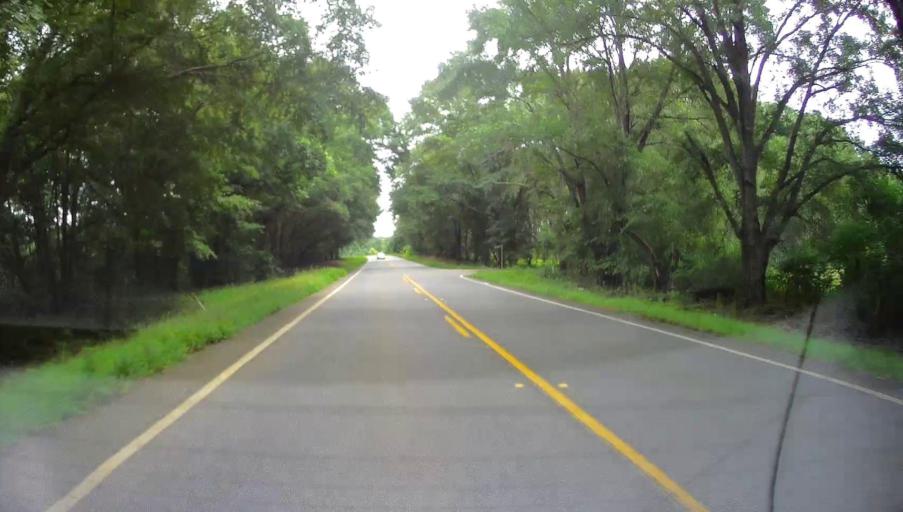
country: US
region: Georgia
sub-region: Schley County
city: Ellaville
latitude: 32.2538
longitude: -84.4026
